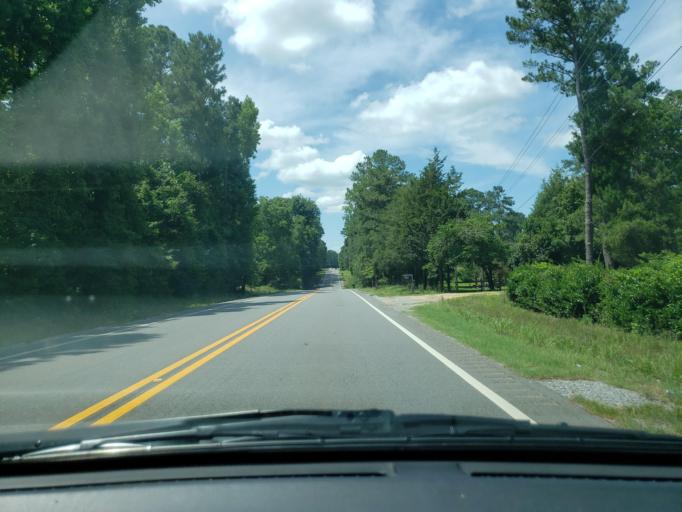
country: US
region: Alabama
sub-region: Elmore County
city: Eclectic
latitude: 32.6281
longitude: -85.9509
